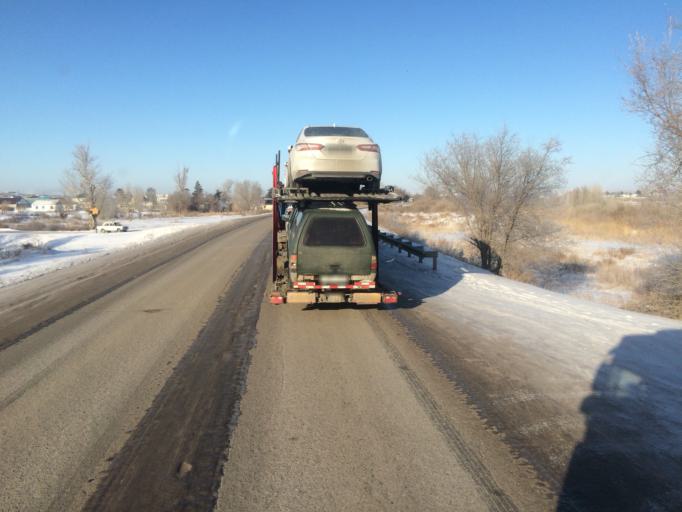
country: KZ
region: Aqtoebe
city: Aqtobe
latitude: 50.2731
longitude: 57.2626
